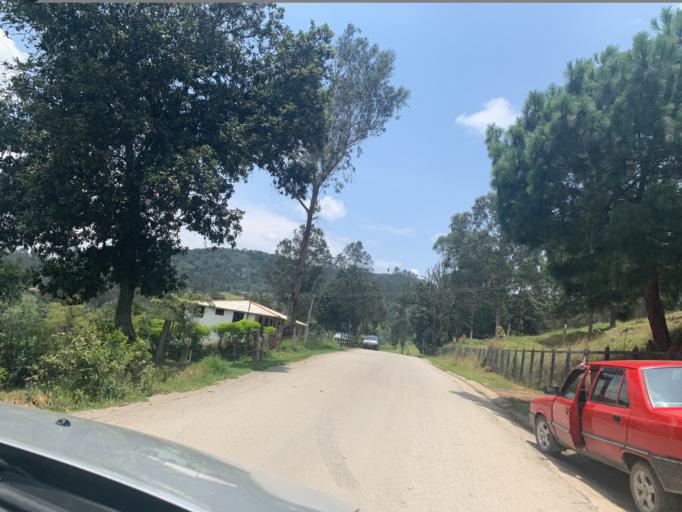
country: CO
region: Boyaca
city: Chiquinquira
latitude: 5.5523
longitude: -73.7499
